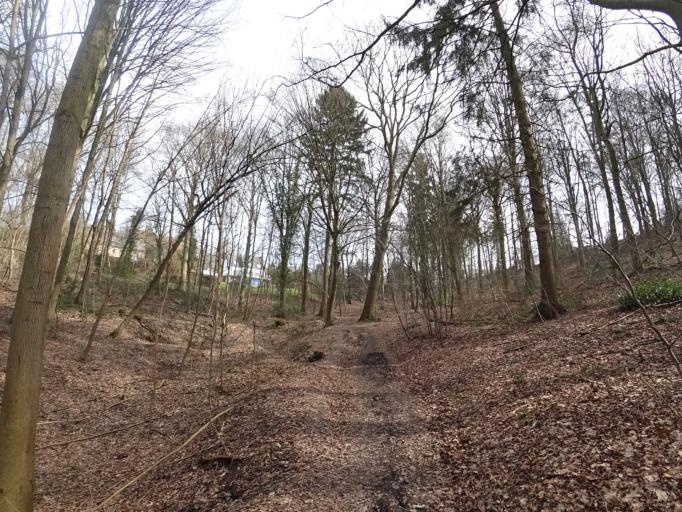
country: BE
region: Wallonia
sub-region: Province de Namur
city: Namur
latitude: 50.4488
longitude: 4.8469
